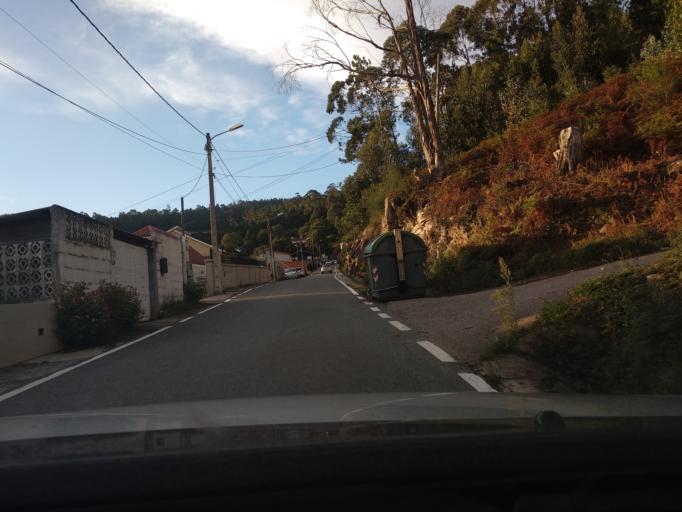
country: ES
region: Galicia
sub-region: Provincia de Pontevedra
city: Redondela
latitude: 42.2931
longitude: -8.6745
